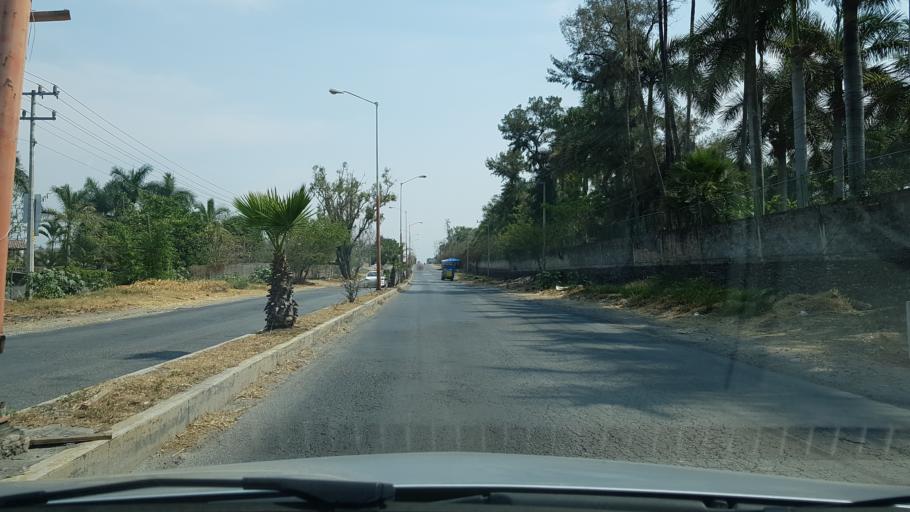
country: MX
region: Morelos
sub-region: Xochitepec
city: Chiconcuac
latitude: 18.7899
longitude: -99.2033
